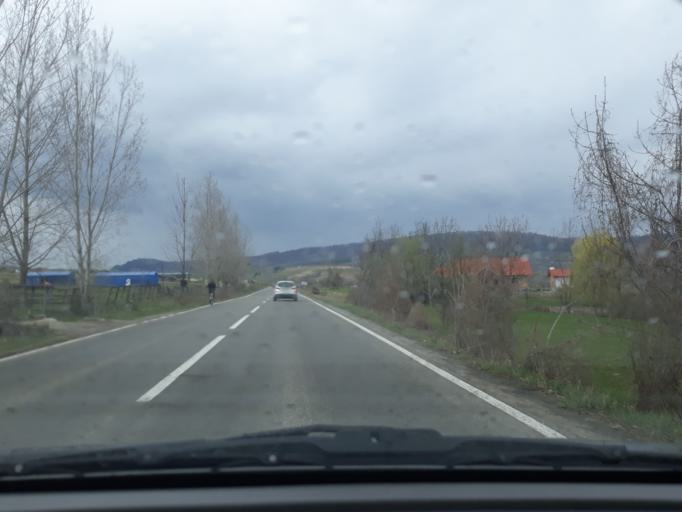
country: RO
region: Harghita
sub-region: Comuna Lupeni
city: Lupeni
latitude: 46.3851
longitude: 25.2179
